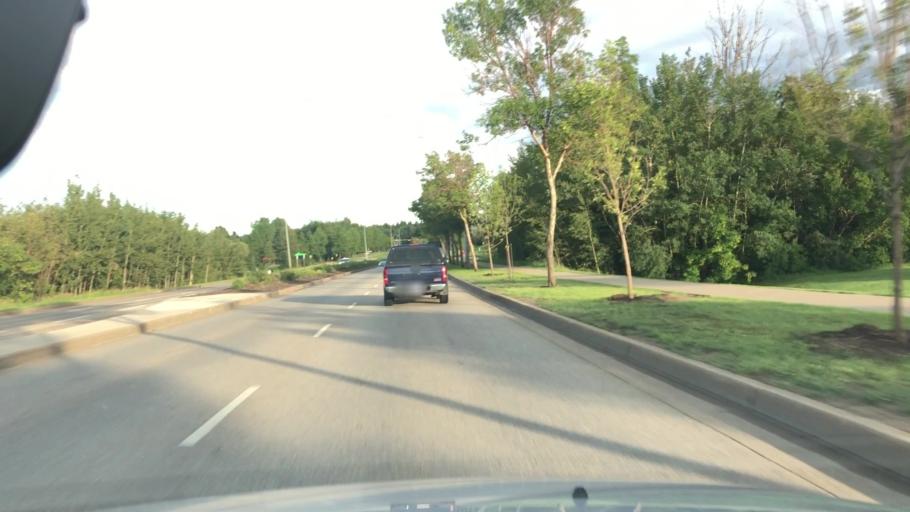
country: CA
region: Alberta
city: St. Albert
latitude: 53.6490
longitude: -113.6160
